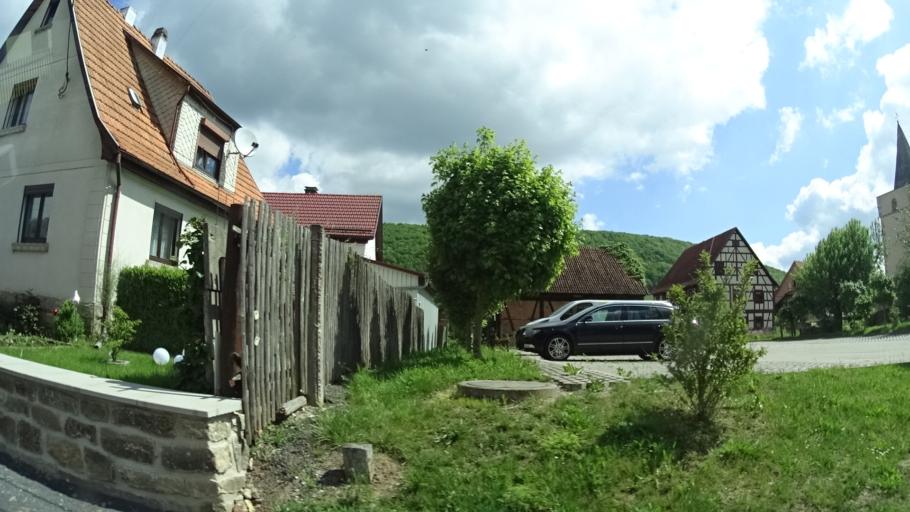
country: DE
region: Thuringia
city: Ritschenhausen
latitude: 50.5099
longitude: 10.4323
